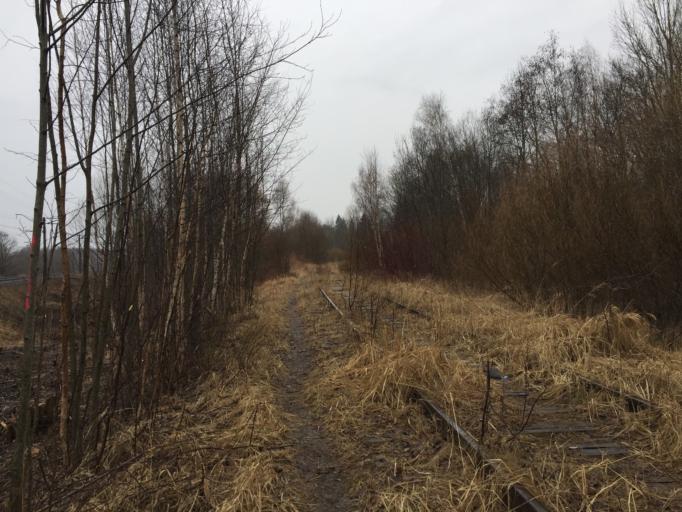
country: LV
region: Lielvarde
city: Lielvarde
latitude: 56.7255
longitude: 24.7824
